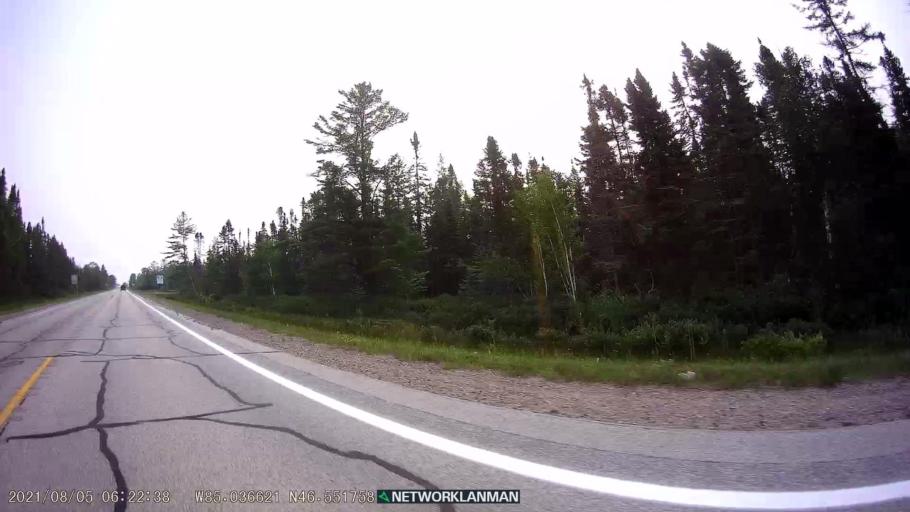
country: US
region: Michigan
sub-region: Luce County
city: Newberry
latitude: 46.5524
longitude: -85.0356
